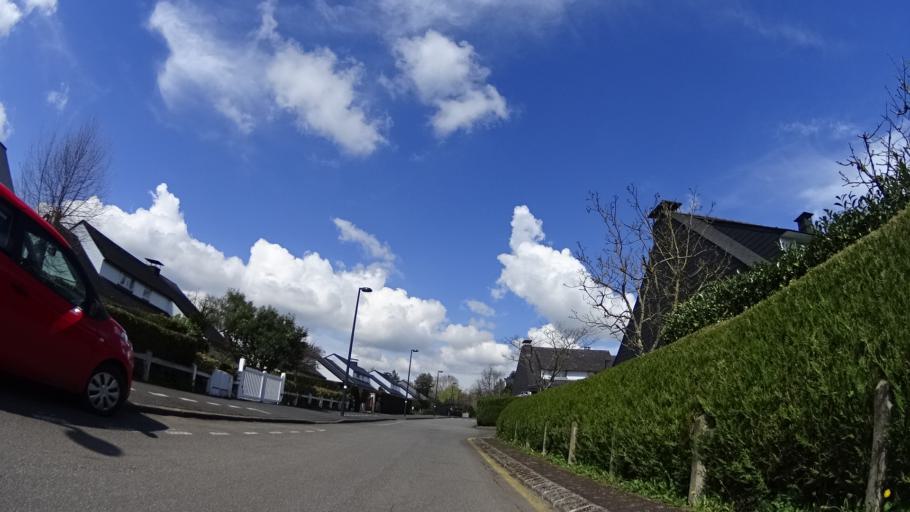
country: FR
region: Brittany
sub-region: Departement d'Ille-et-Vilaine
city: Saint-Gregoire
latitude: 48.1332
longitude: -1.6764
